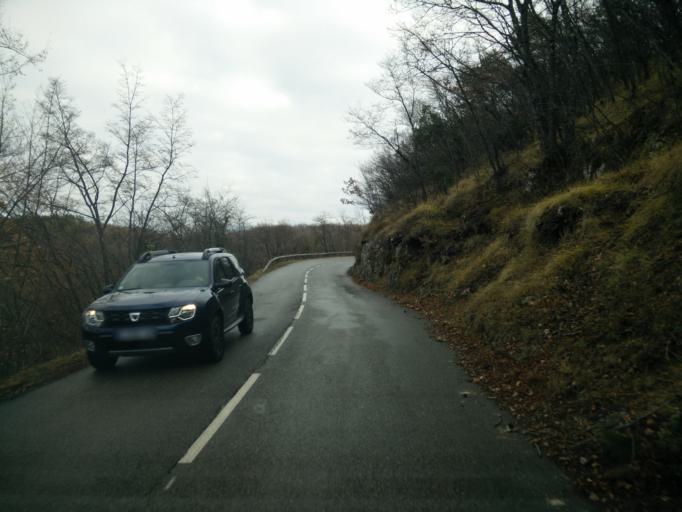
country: FR
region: Provence-Alpes-Cote d'Azur
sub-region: Departement des Alpes-Maritimes
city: Le Broc
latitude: 43.8243
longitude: 7.1479
